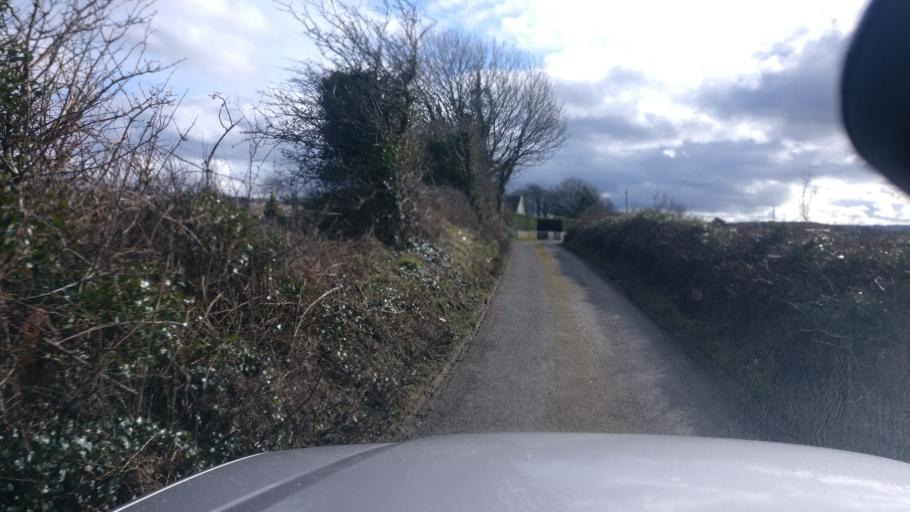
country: IE
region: Connaught
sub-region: County Galway
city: Loughrea
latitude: 53.1949
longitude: -8.5406
